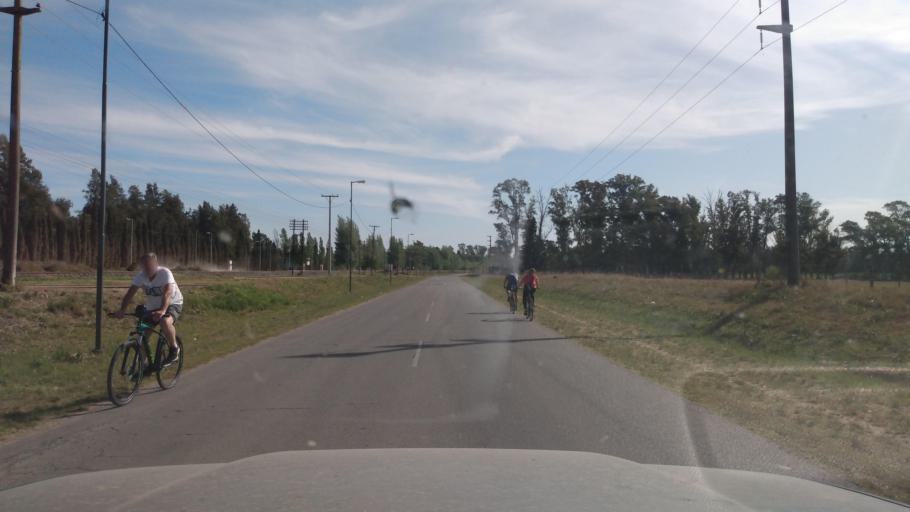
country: AR
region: Buenos Aires
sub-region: Partido de Lujan
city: Lujan
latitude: -34.5922
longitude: -59.1473
